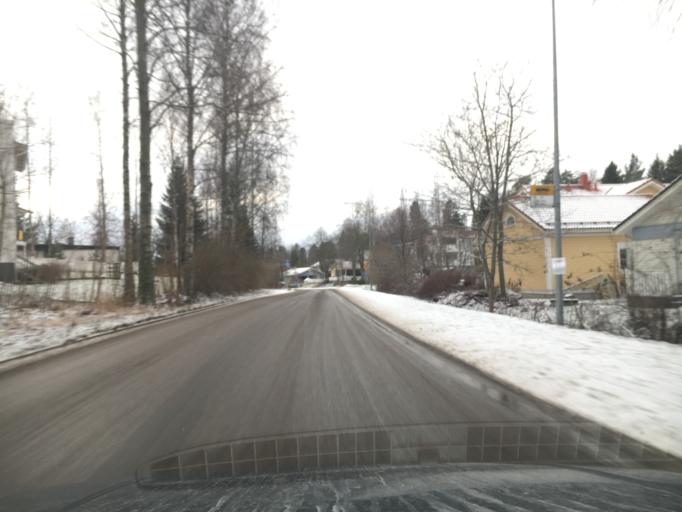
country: FI
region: Uusimaa
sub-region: Helsinki
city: Espoo
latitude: 60.1632
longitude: 24.6499
